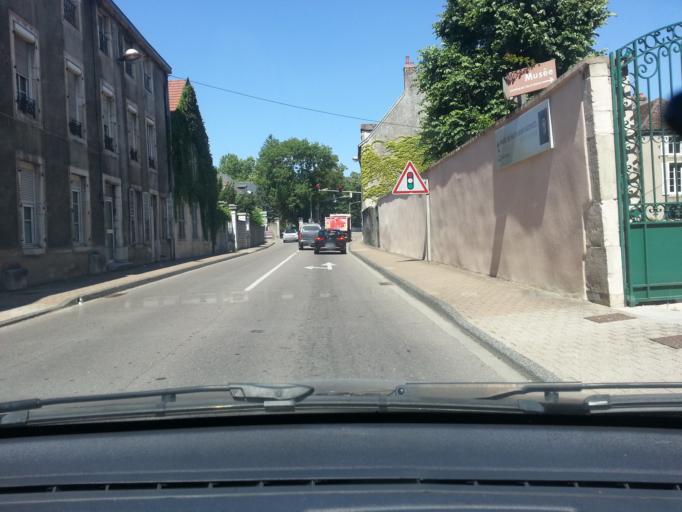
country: FR
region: Bourgogne
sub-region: Departement de la Cote-d'Or
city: Nuits-Saint-Georges
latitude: 47.1387
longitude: 4.9504
